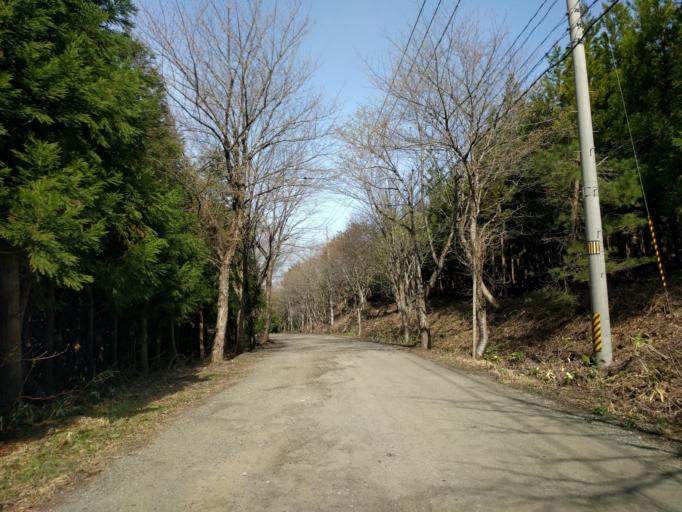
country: JP
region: Fukushima
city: Inawashiro
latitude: 37.5273
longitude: 140.0353
